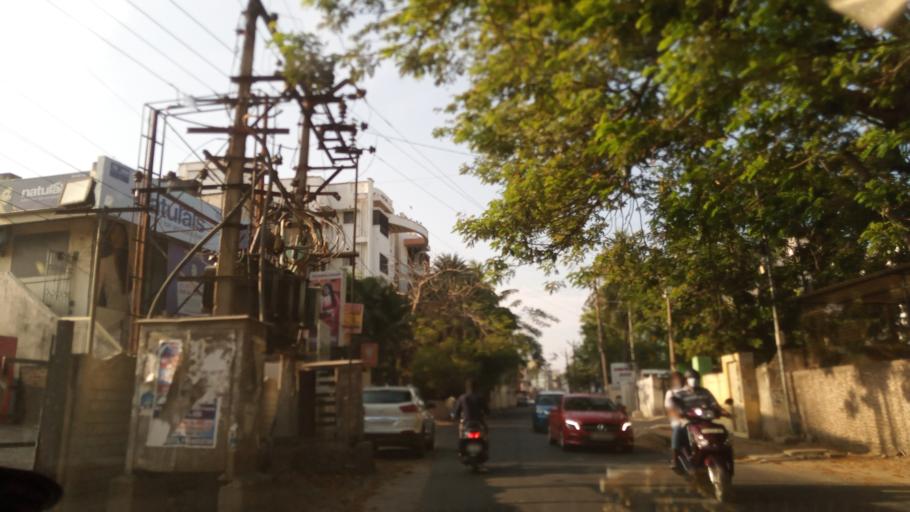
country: IN
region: Tamil Nadu
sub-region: Kancheepuram
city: Manappakkam
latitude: 13.0249
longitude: 80.1831
